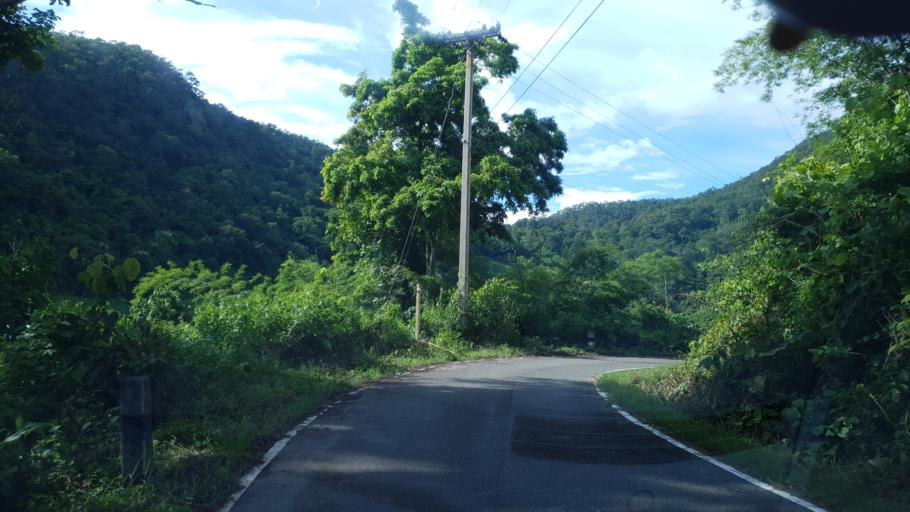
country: TH
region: Mae Hong Son
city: Khun Yuam
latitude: 18.6544
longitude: 97.9439
